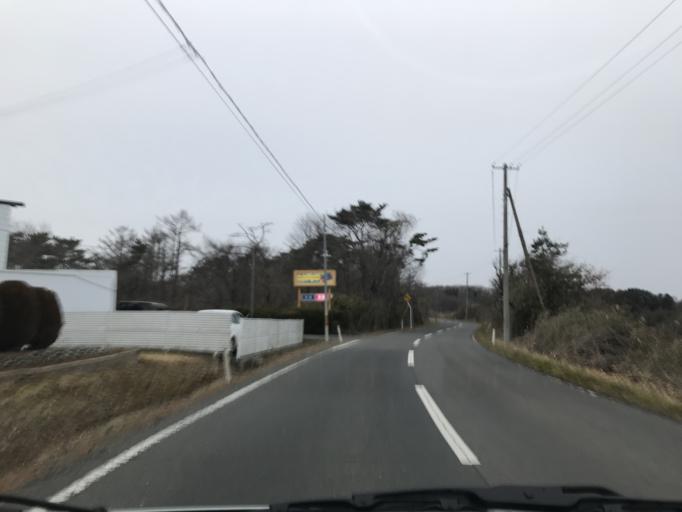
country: JP
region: Miyagi
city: Wakuya
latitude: 38.6738
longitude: 141.1045
